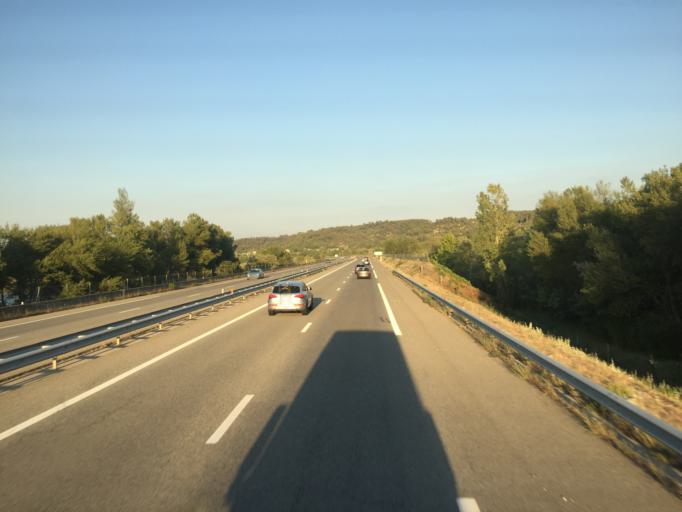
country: FR
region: Provence-Alpes-Cote d'Azur
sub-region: Departement du Vaucluse
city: Beaumont-de-Pertuis
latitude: 43.6893
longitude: 5.7022
